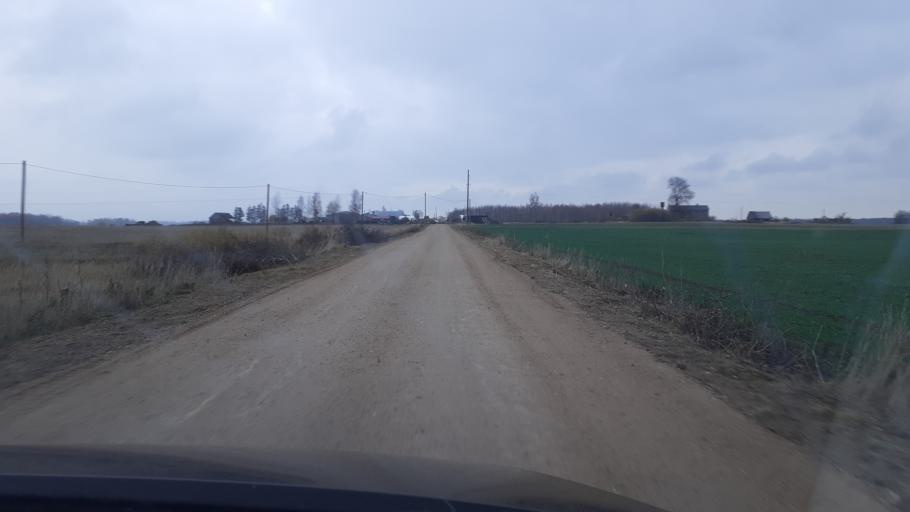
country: LV
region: Talsu Rajons
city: Sabile
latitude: 56.9376
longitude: 22.4186
